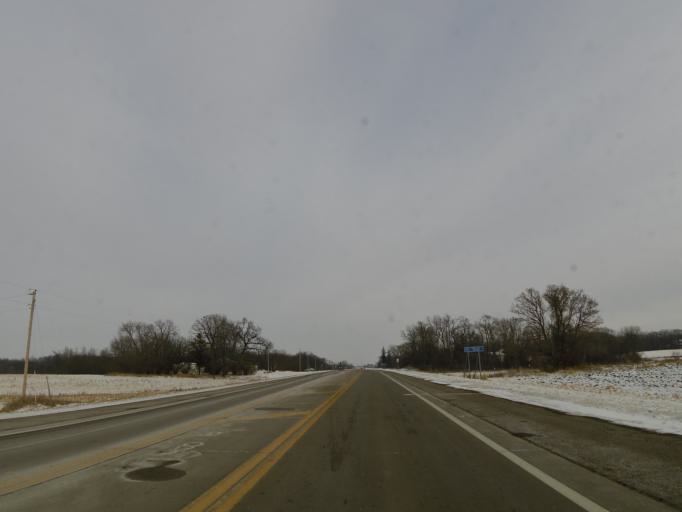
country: US
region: Minnesota
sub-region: McLeod County
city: Hutchinson
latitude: 44.8926
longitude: -94.2800
